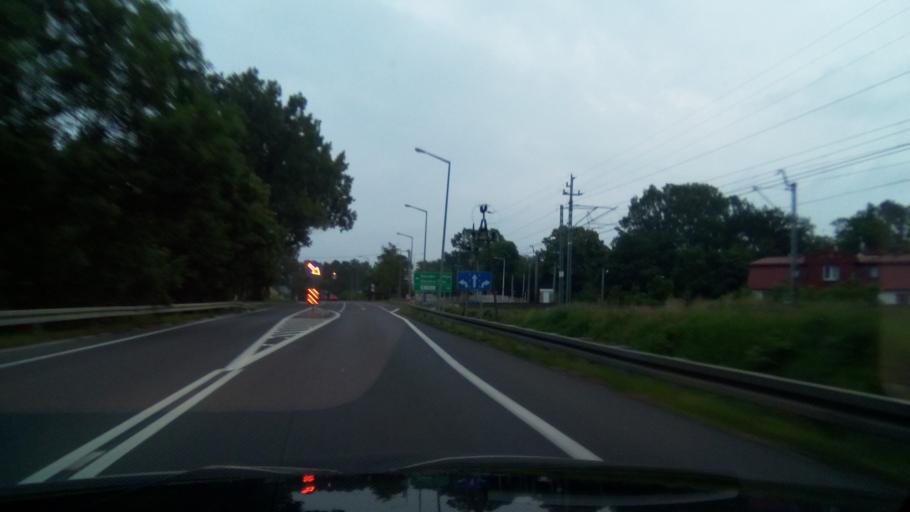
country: PL
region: Greater Poland Voivodeship
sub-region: Powiat poznanski
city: Kostrzyn
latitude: 52.4715
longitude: 17.2114
